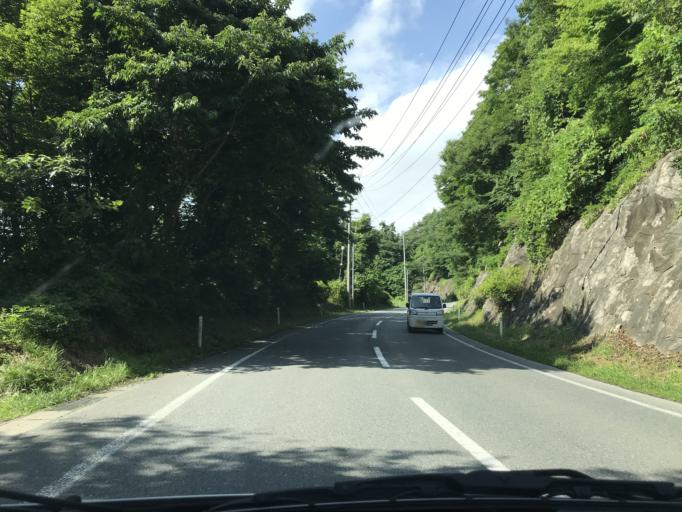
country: JP
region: Iwate
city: Ichinoseki
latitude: 38.9998
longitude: 141.2692
